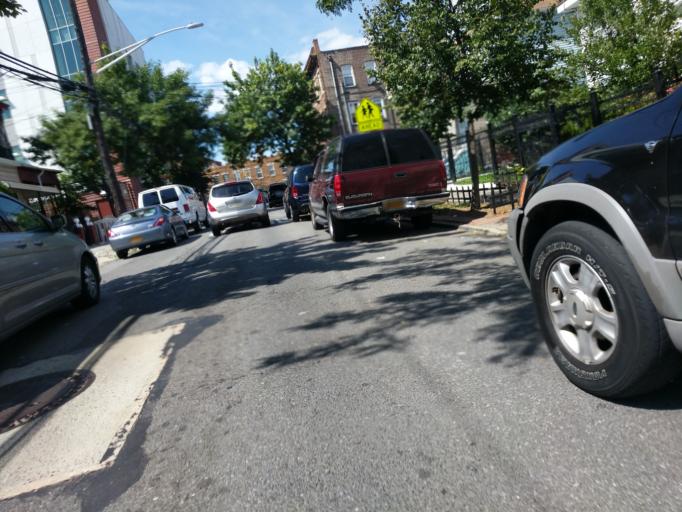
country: US
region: New York
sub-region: Queens County
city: Borough of Queens
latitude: 40.7573
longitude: -73.8583
